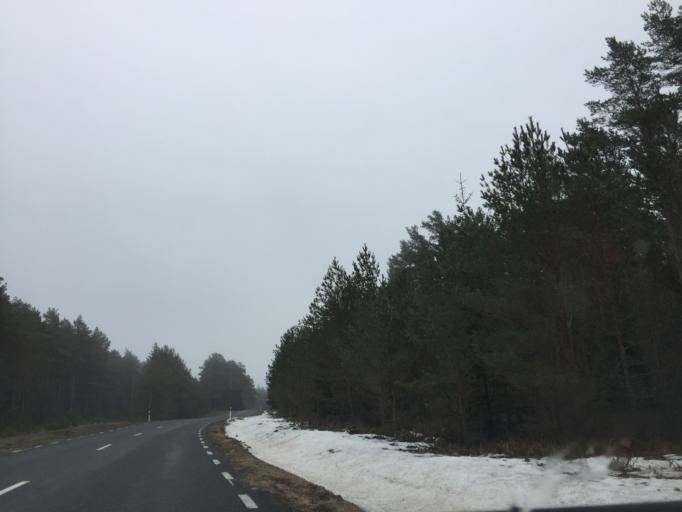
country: EE
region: Saare
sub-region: Kuressaare linn
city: Kuressaare
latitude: 58.4690
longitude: 22.0266
